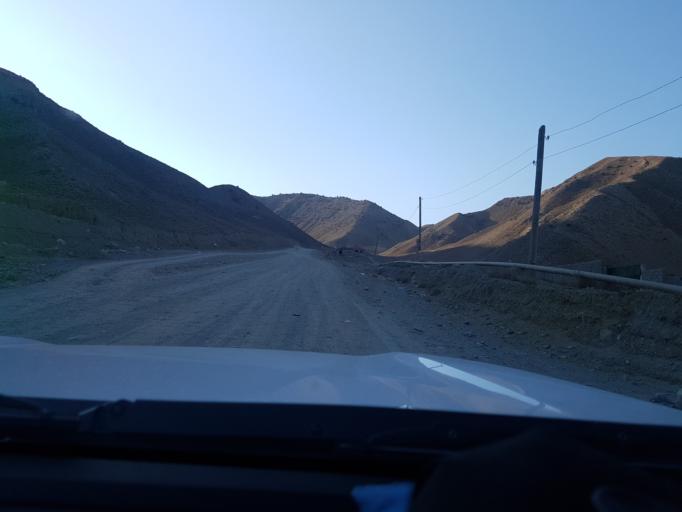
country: TM
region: Ahal
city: Baharly
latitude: 38.4529
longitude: 57.0455
